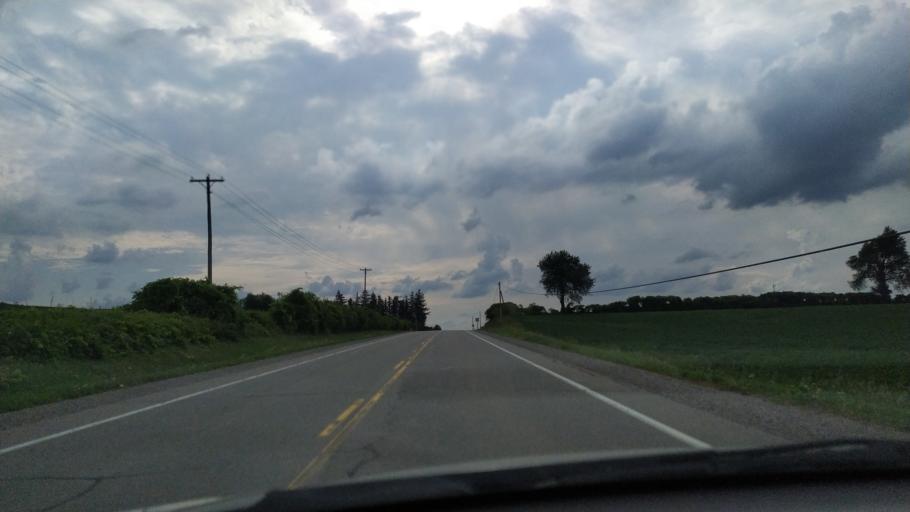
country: CA
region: Ontario
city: Kitchener
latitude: 43.3550
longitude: -80.4989
